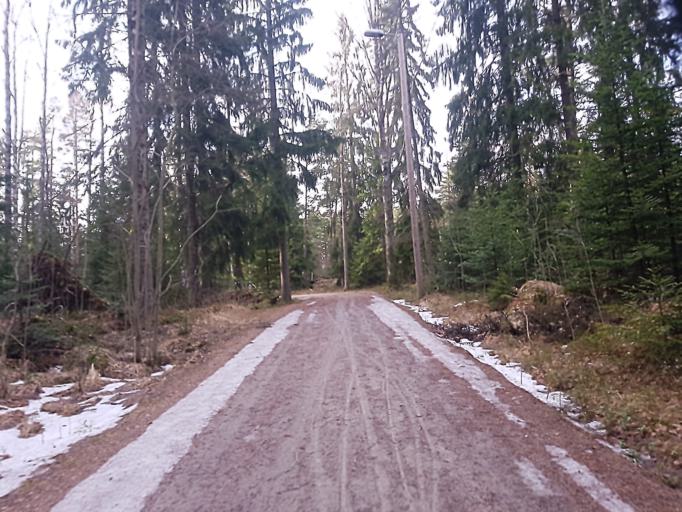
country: FI
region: Uusimaa
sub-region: Helsinki
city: Helsinki
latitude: 60.2684
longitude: 24.9158
